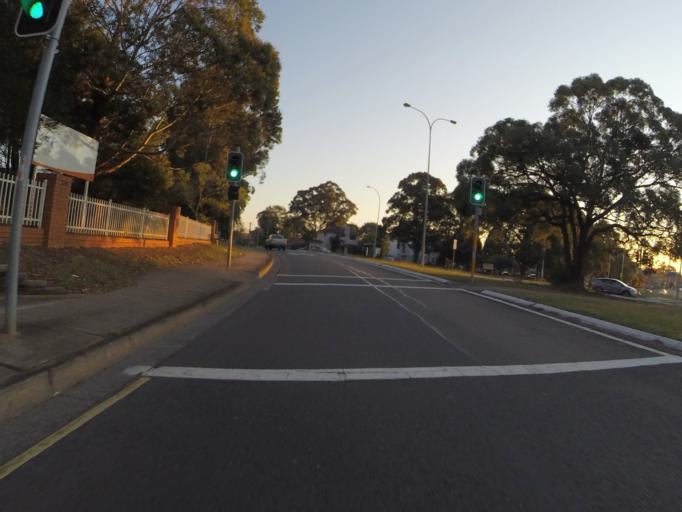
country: AU
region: New South Wales
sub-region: Hurstville
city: Peakhurst
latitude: -33.9614
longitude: 151.0585
